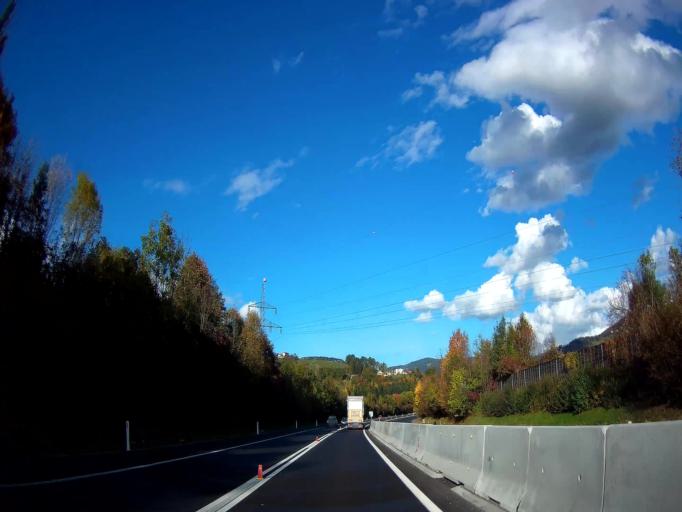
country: AT
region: Carinthia
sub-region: Politischer Bezirk Wolfsberg
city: Wolfsberg
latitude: 46.8405
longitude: 14.8237
